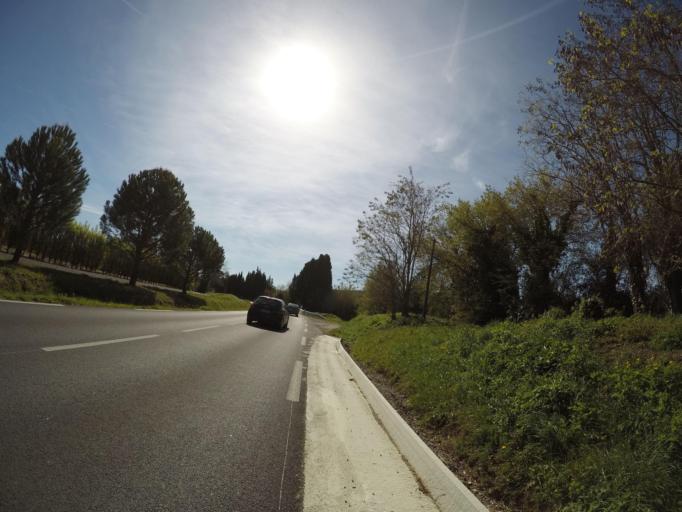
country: FR
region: Languedoc-Roussillon
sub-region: Departement des Pyrenees-Orientales
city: Millas
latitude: 42.6467
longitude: 2.7083
